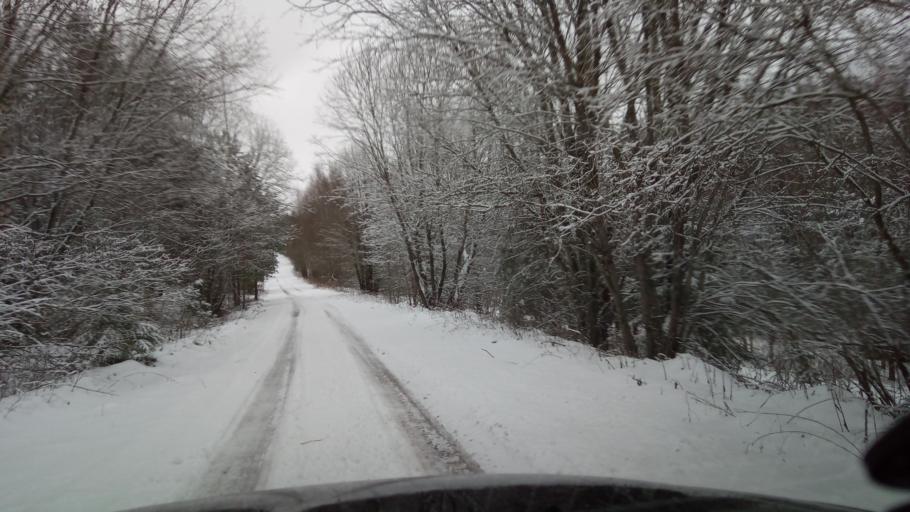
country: LT
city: Zarasai
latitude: 55.6642
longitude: 26.0904
